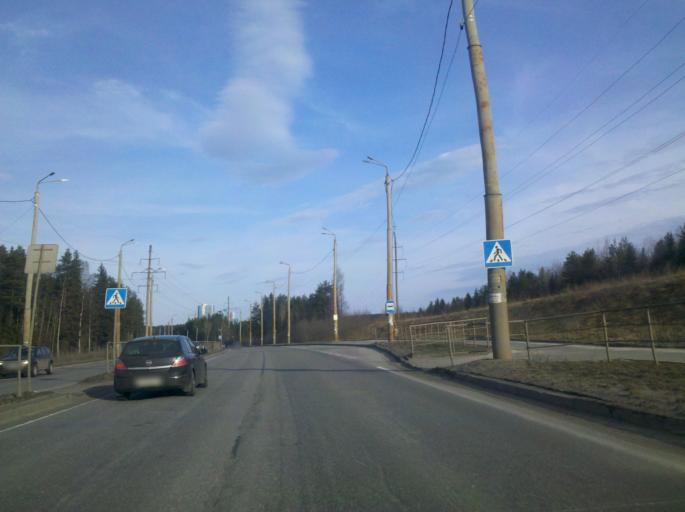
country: RU
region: Republic of Karelia
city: Petrozavodsk
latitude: 61.7592
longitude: 34.3329
